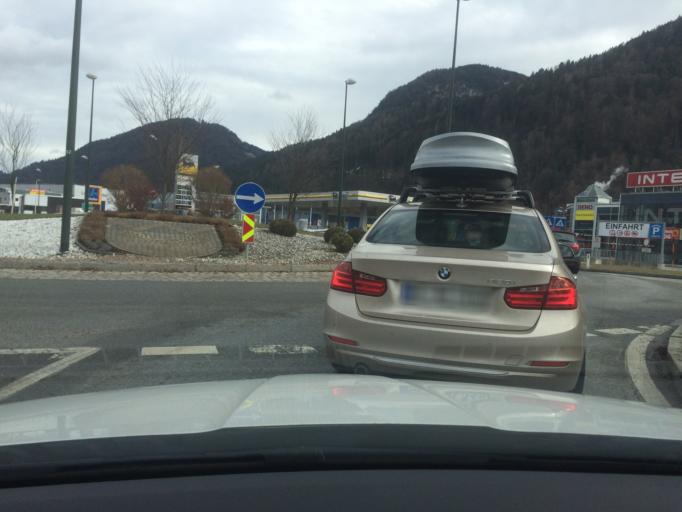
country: AT
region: Tyrol
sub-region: Politischer Bezirk Kufstein
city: Worgl
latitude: 47.4779
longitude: 12.0445
